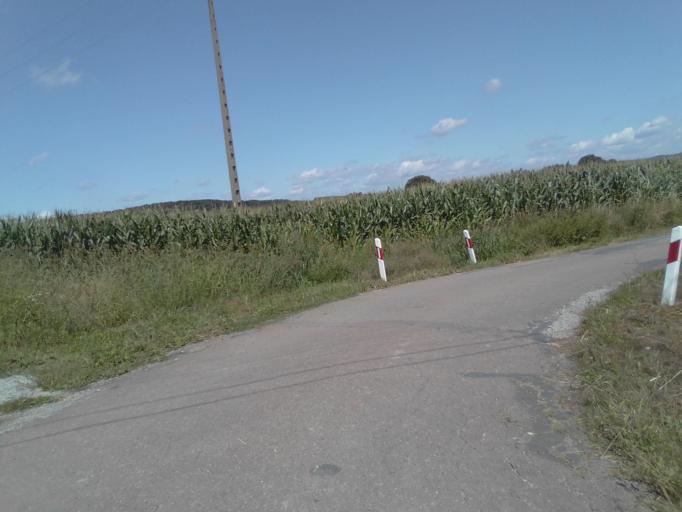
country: PL
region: Subcarpathian Voivodeship
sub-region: Powiat krosnienski
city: Wojaszowka
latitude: 49.7634
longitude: 21.6434
